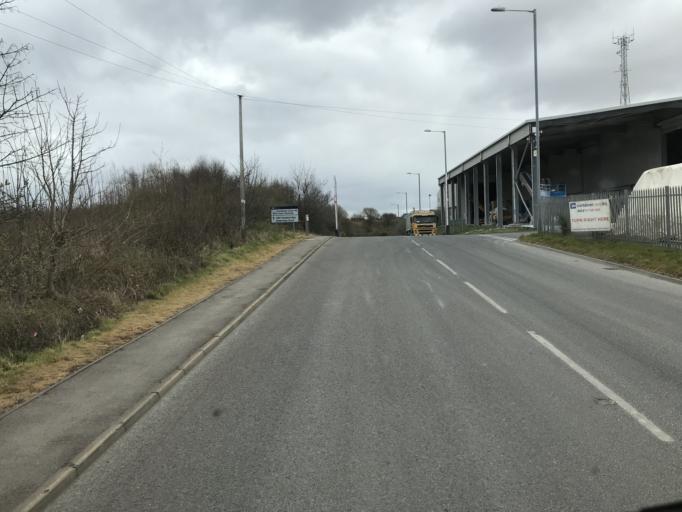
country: GB
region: England
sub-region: Cheshire West and Chester
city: Ellesmere Port
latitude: 53.3519
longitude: -2.9060
